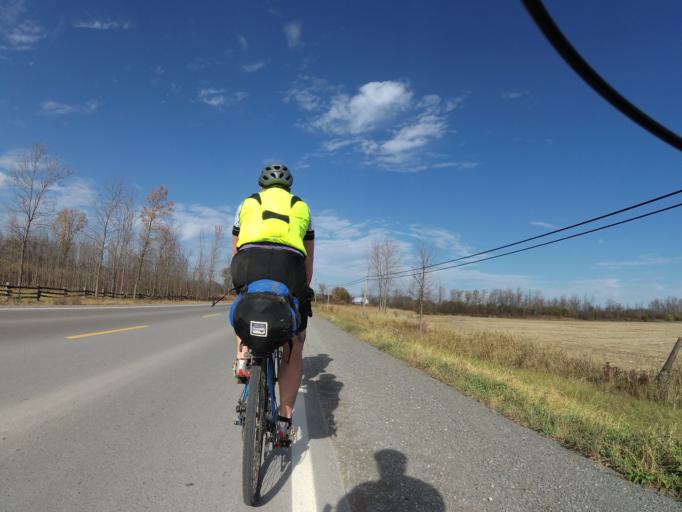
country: CA
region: Ontario
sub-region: Lanark County
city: Smiths Falls
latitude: 44.8692
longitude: -75.9787
